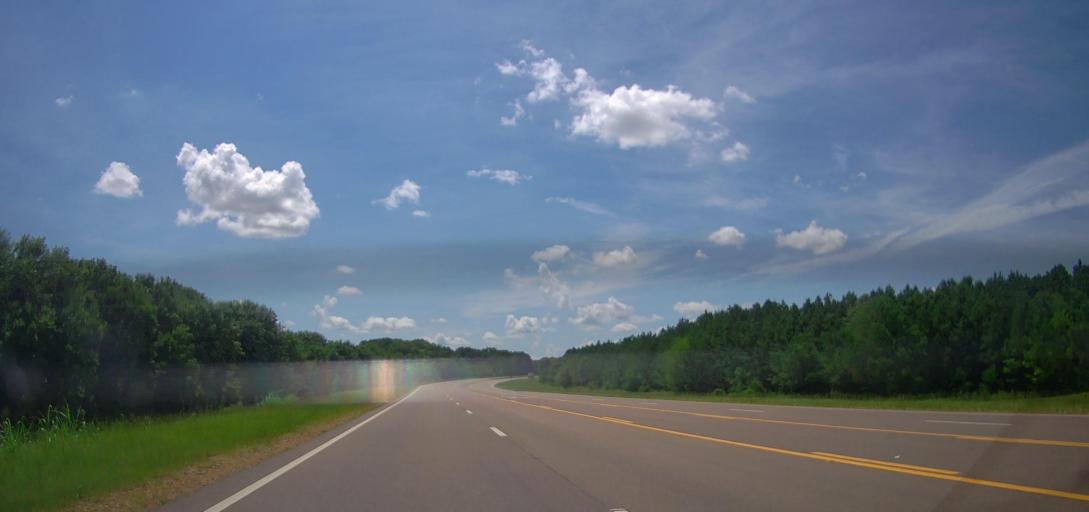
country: US
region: Mississippi
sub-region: Monroe County
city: Aberdeen
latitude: 33.8147
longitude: -88.5680
